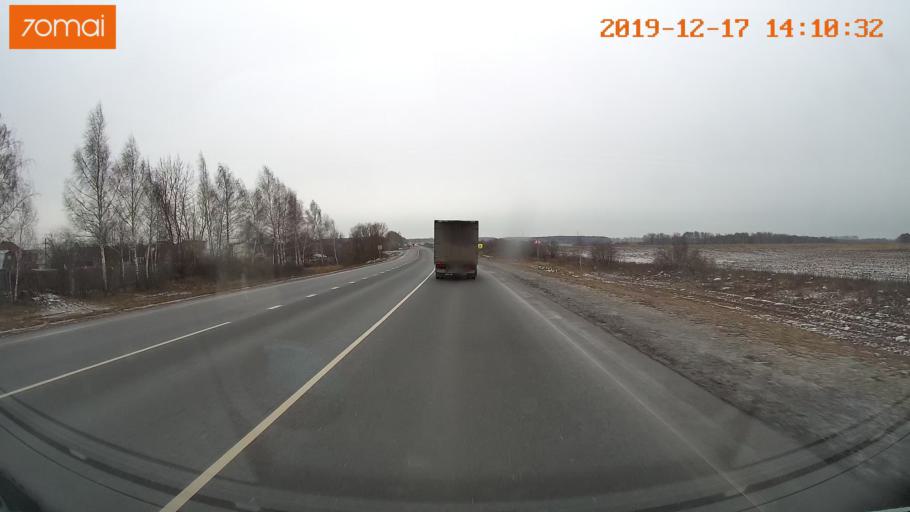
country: RU
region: Rjazan
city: Rybnoye
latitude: 54.5471
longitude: 39.5176
